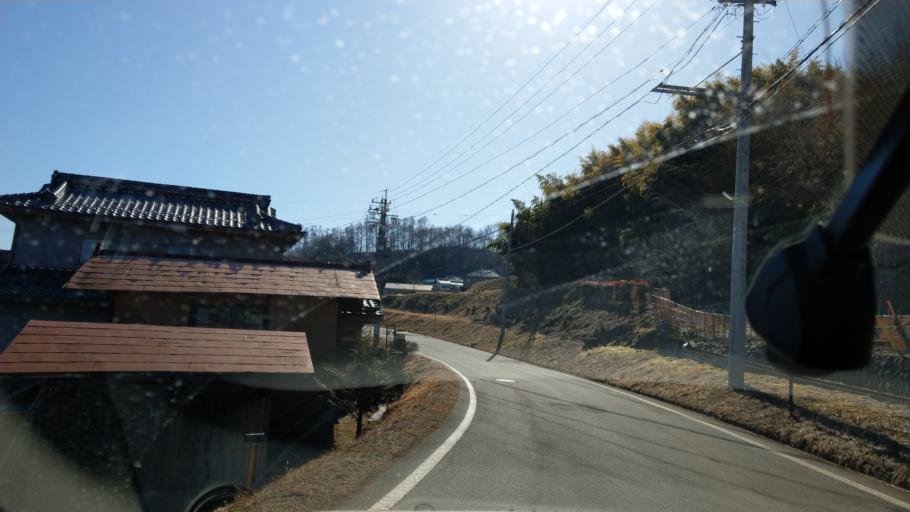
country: JP
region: Nagano
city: Saku
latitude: 36.2224
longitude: 138.4458
